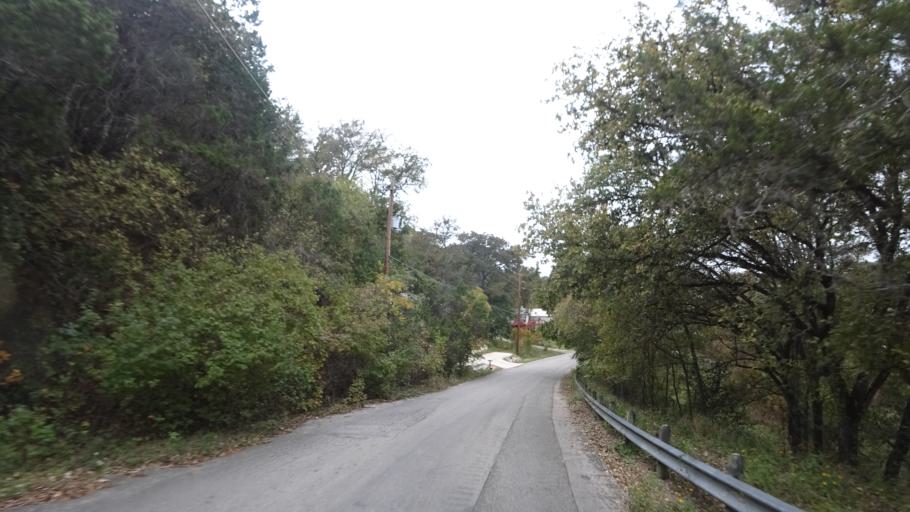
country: US
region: Texas
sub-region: Travis County
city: Hudson Bend
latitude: 30.3757
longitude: -97.9168
